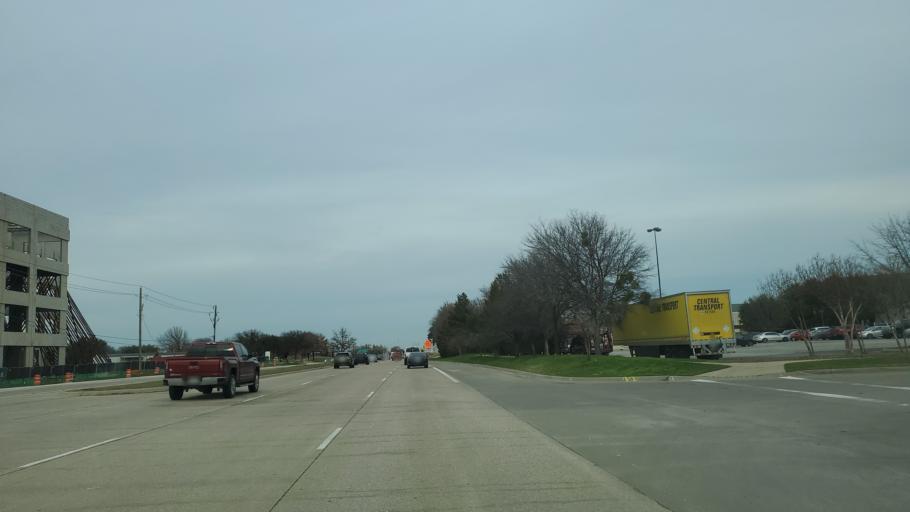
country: US
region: Texas
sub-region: Dallas County
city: Coppell
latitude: 32.9567
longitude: -97.0464
